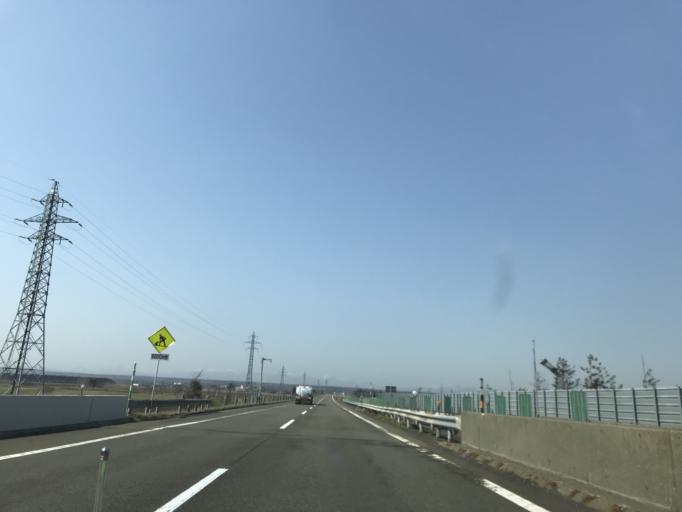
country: JP
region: Hokkaido
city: Ebetsu
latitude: 43.0913
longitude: 141.5734
